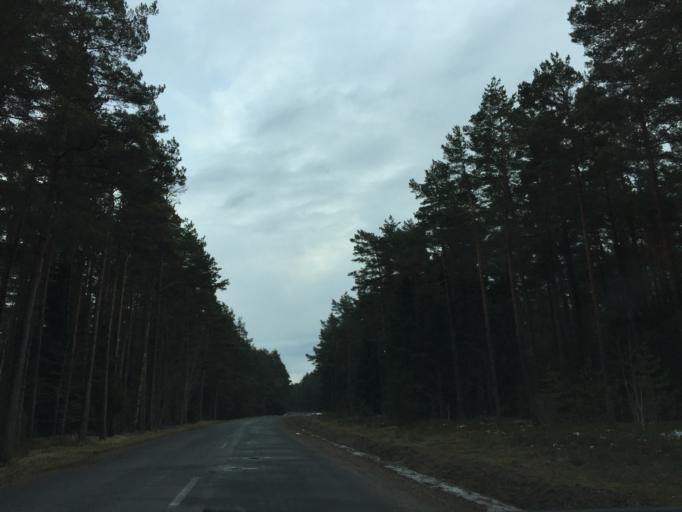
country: EE
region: Saare
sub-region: Kuressaare linn
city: Kuressaare
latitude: 58.4375
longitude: 22.0619
